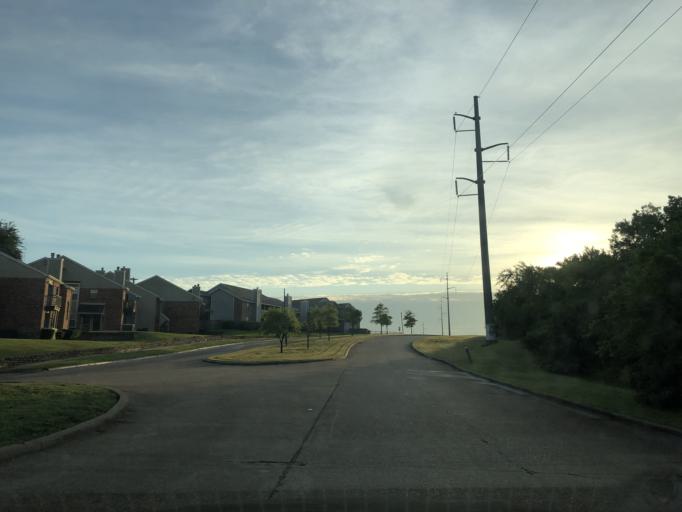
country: US
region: Texas
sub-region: Dallas County
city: Garland
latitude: 32.8403
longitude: -96.6217
